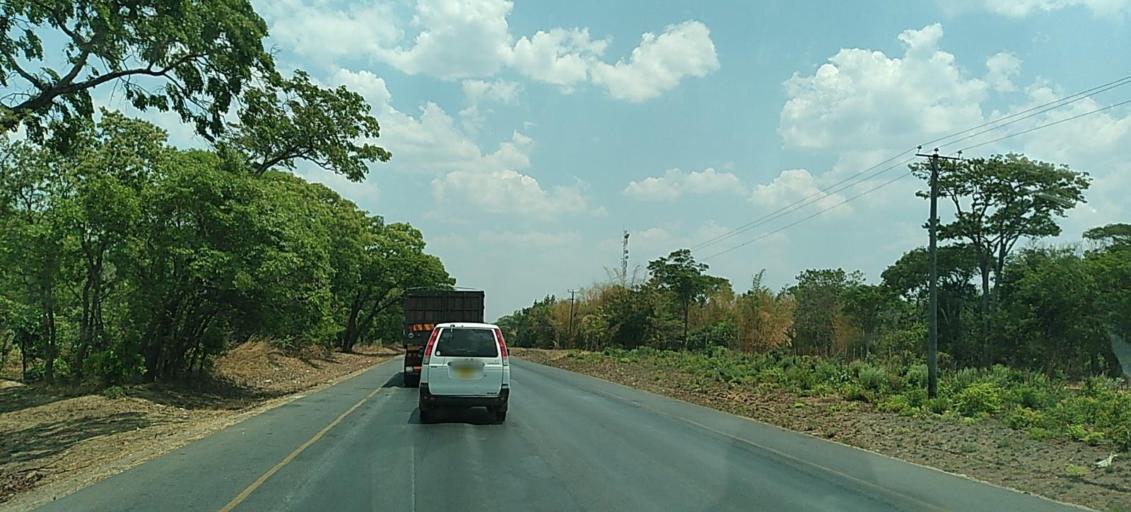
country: ZM
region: Central
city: Kapiri Mposhi
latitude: -14.2032
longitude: 28.5862
